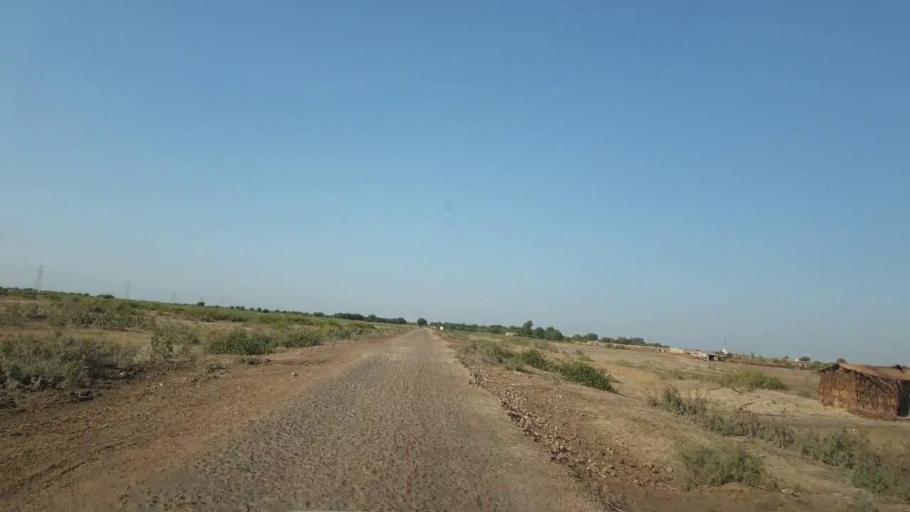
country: PK
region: Sindh
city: Kunri
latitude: 25.0425
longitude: 69.4421
